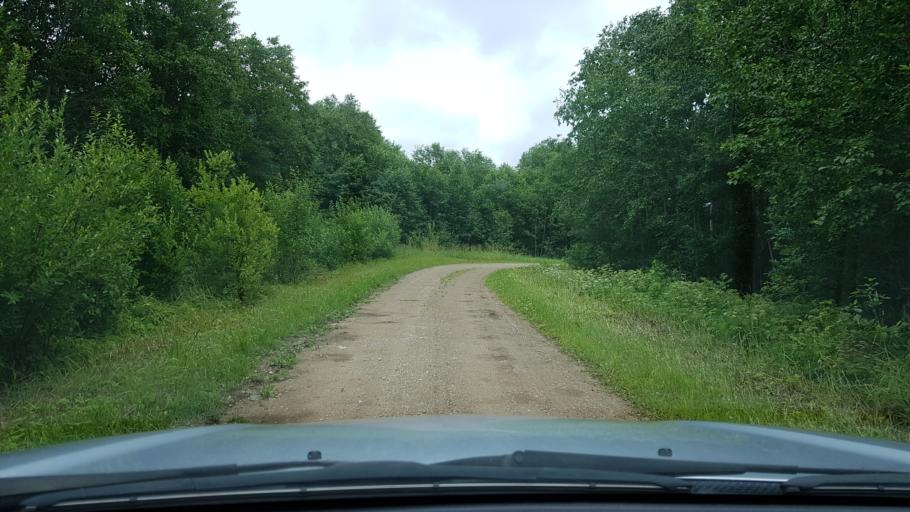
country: EE
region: Ida-Virumaa
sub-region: Narva-Joesuu linn
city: Narva-Joesuu
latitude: 59.3432
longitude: 27.9636
